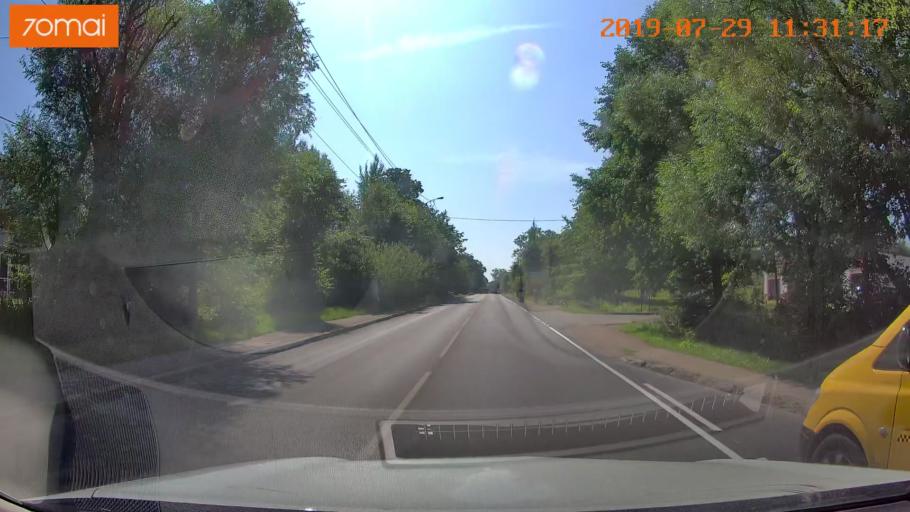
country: RU
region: Kaliningrad
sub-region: Gorod Kaliningrad
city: Kaliningrad
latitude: 54.6761
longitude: 20.5407
